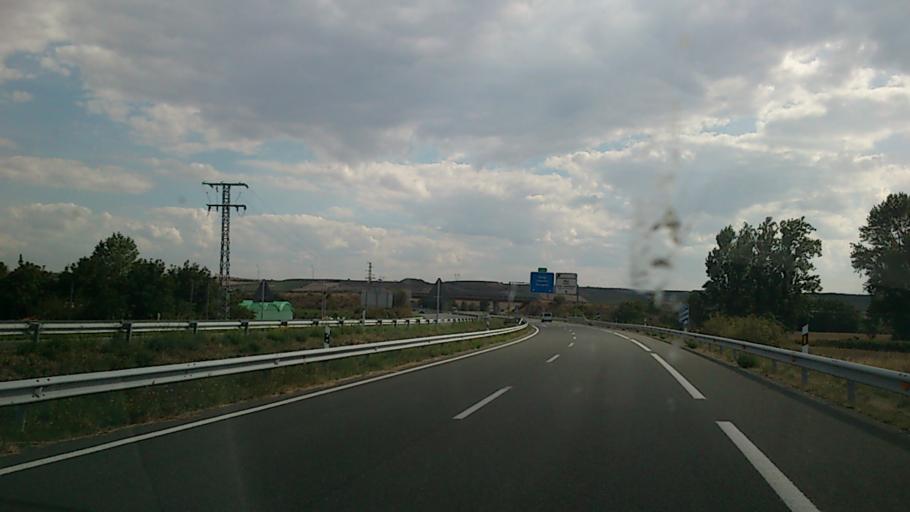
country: ES
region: La Rioja
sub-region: Provincia de La Rioja
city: Anguciana
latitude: 42.5654
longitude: -2.8802
